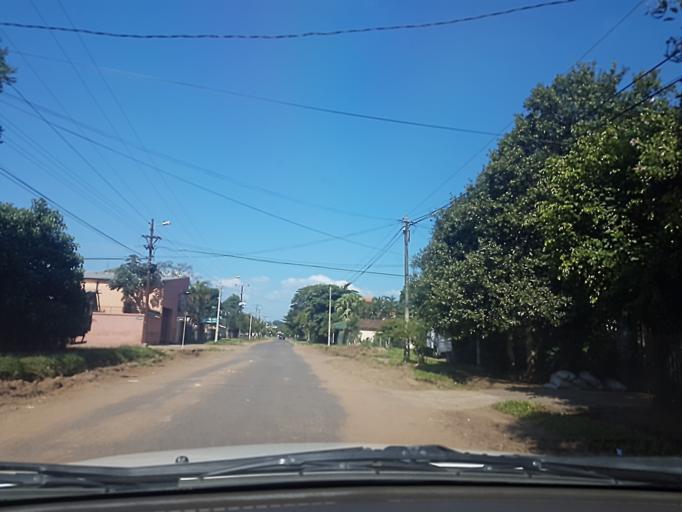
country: PY
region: Central
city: Limpio
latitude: -25.1748
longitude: -57.4792
